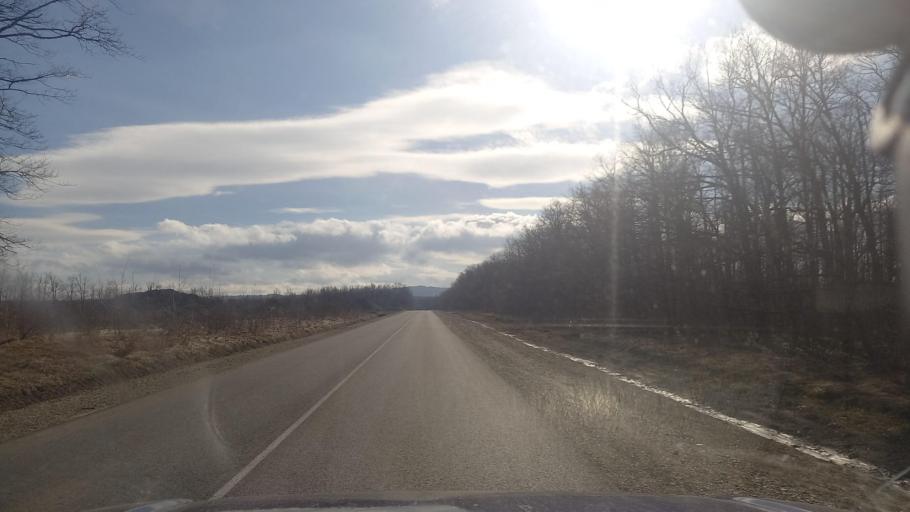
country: RU
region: Krasnodarskiy
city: Novodmitriyevskaya
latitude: 44.7348
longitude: 38.9954
